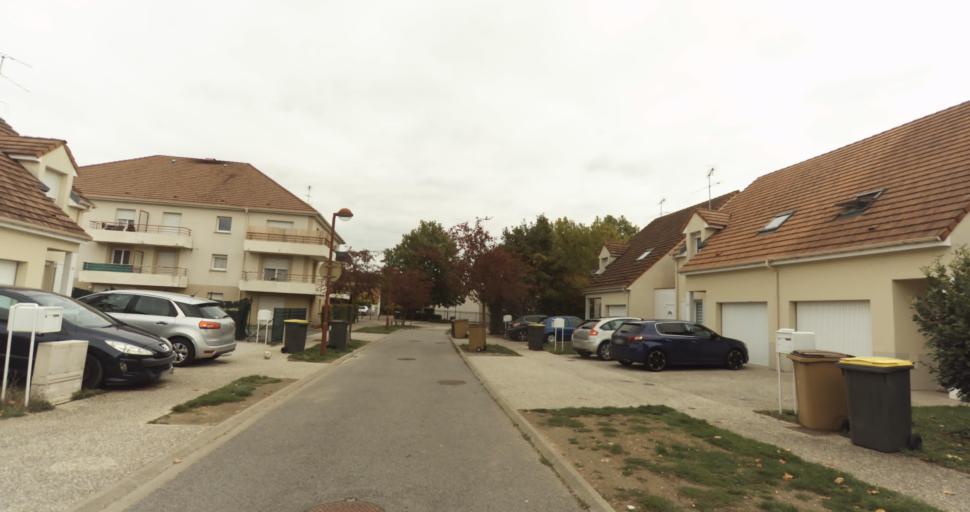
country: FR
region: Centre
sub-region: Departement d'Eure-et-Loir
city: Garnay
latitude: 48.7277
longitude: 1.3419
